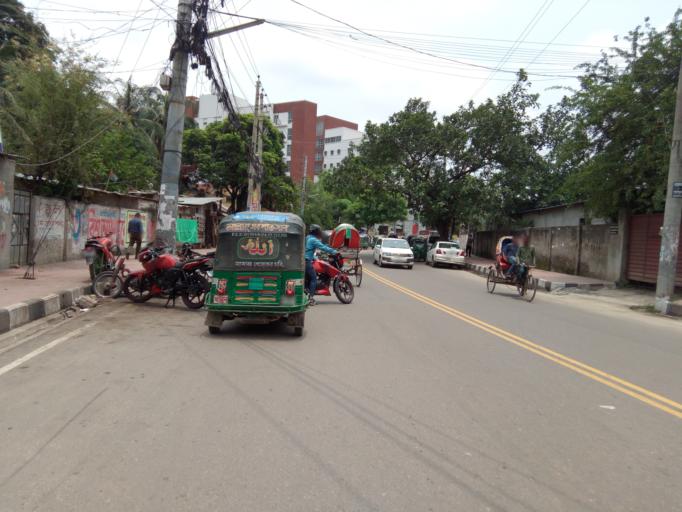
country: BD
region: Dhaka
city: Paltan
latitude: 23.7648
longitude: 90.4062
